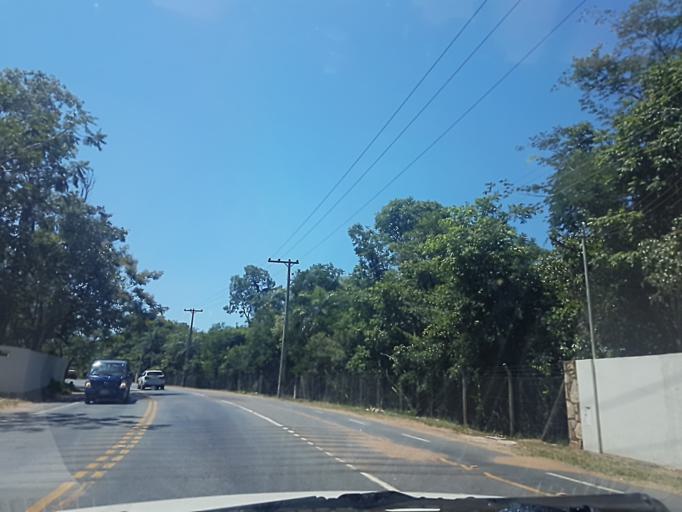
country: PY
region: Cordillera
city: San Bernardino
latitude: -25.2505
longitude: -57.3216
